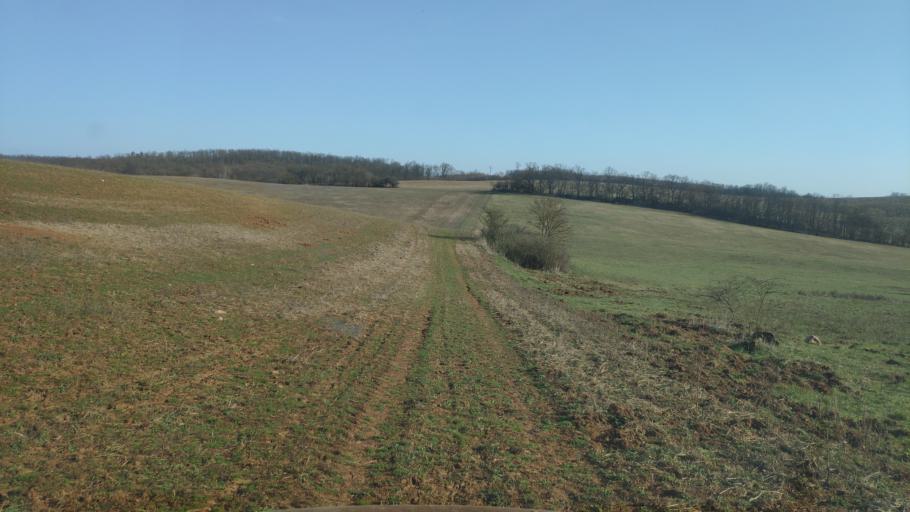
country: SK
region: Banskobystricky
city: Revuca
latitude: 48.5467
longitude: 20.2546
